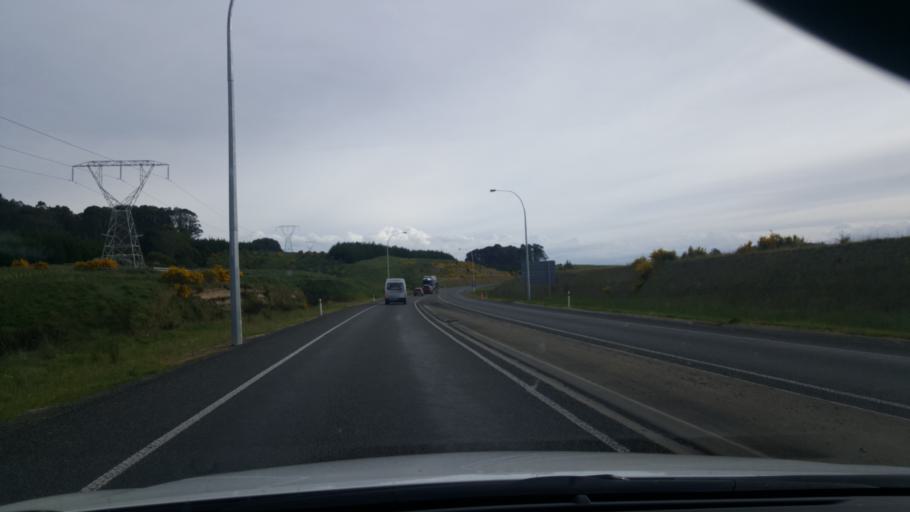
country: NZ
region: Waikato
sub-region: Taupo District
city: Taupo
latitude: -38.7059
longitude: 176.1121
